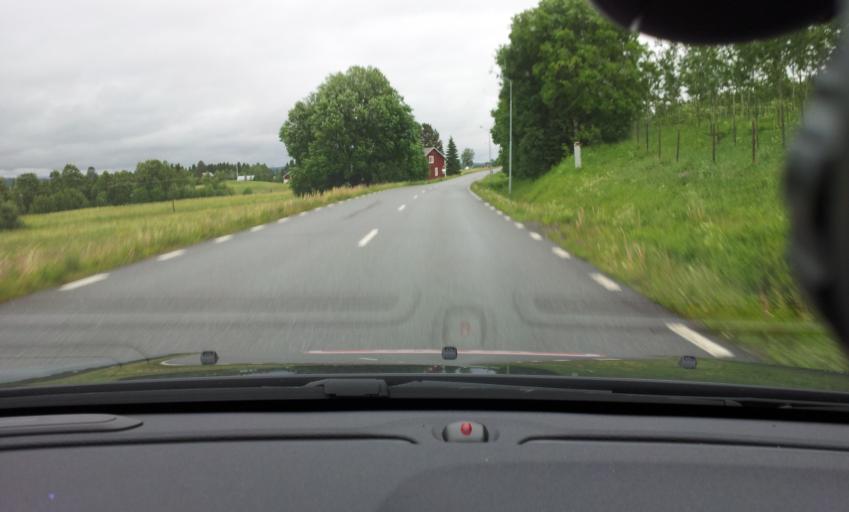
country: SE
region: Jaemtland
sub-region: Stroemsunds Kommun
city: Stroemsund
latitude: 63.5712
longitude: 15.3848
